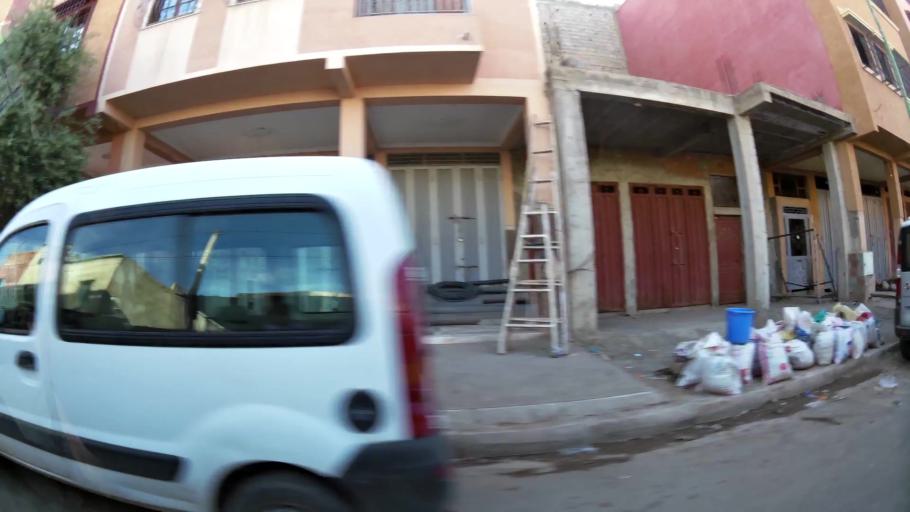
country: MA
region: Marrakech-Tensift-Al Haouz
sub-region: Marrakech
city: Marrakesh
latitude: 31.6877
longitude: -8.0628
